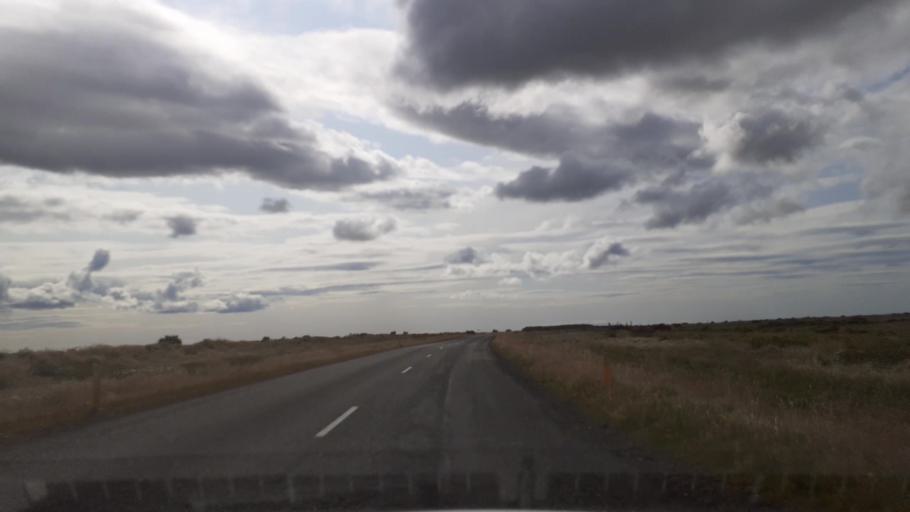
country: IS
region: South
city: Vestmannaeyjar
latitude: 63.8227
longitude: -20.4274
